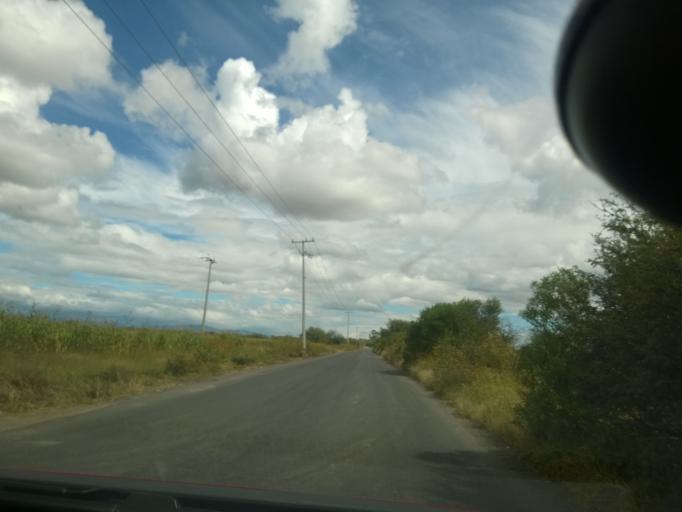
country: MX
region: Guanajuato
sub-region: Leon
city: El CERESO
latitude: 20.9919
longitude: -101.6572
